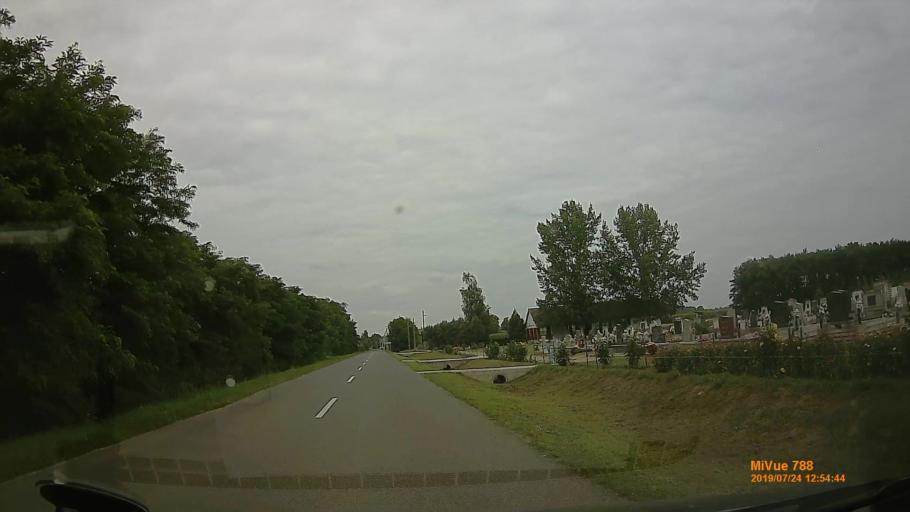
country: HU
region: Szabolcs-Szatmar-Bereg
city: Aranyosapati
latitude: 48.2188
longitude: 22.2963
